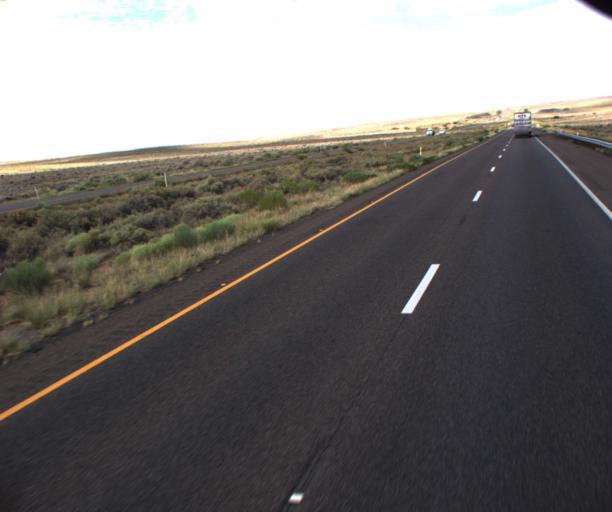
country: US
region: Arizona
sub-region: Navajo County
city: Holbrook
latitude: 35.0875
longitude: -109.6977
